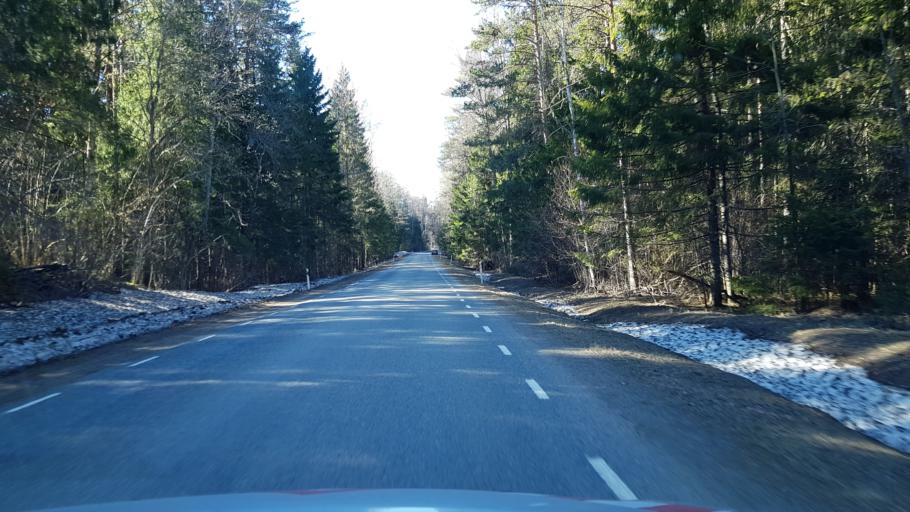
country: EE
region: Laeaene-Virumaa
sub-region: Vinni vald
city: Vinni
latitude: 59.2676
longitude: 26.6687
